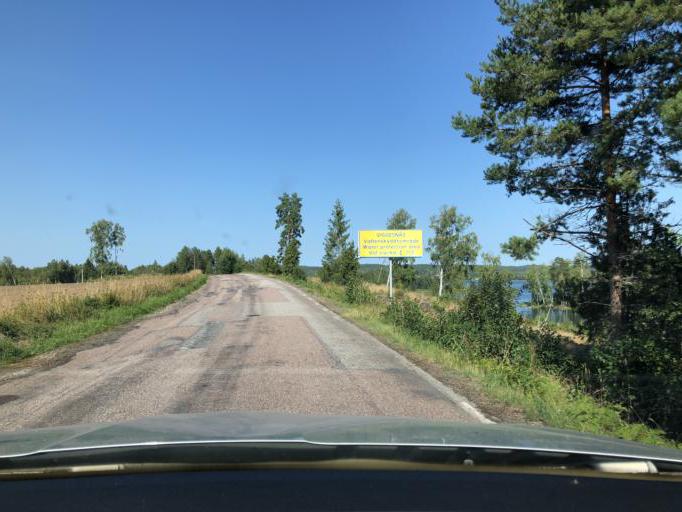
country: SE
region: Dalarna
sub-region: Hedemora Kommun
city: Hedemora
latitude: 60.3303
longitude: 15.9183
